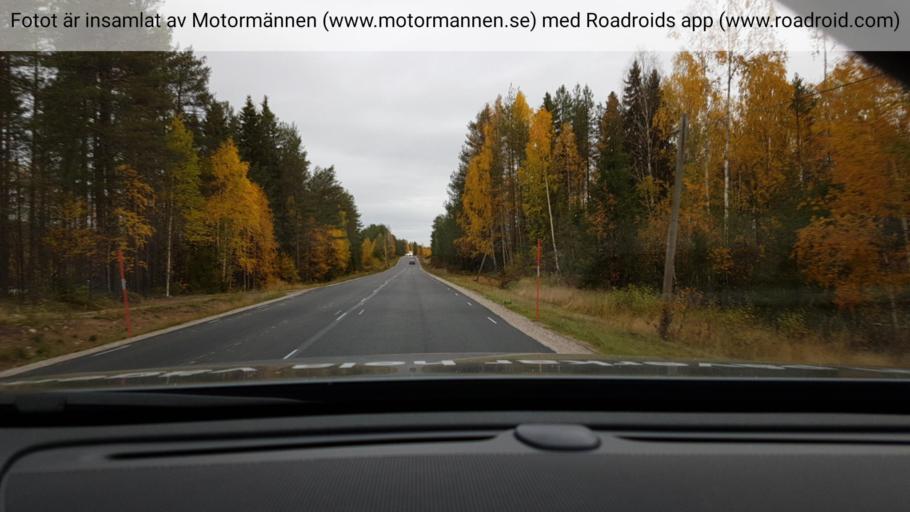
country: SE
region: Norrbotten
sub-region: Overkalix Kommun
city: OEverkalix
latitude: 66.4382
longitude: 22.7909
